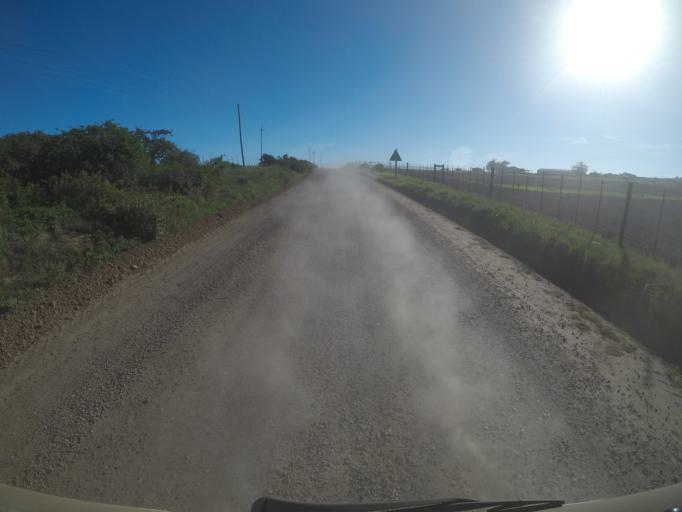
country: ZA
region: Western Cape
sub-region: Eden District Municipality
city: Mossel Bay
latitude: -34.1448
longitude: 22.0029
